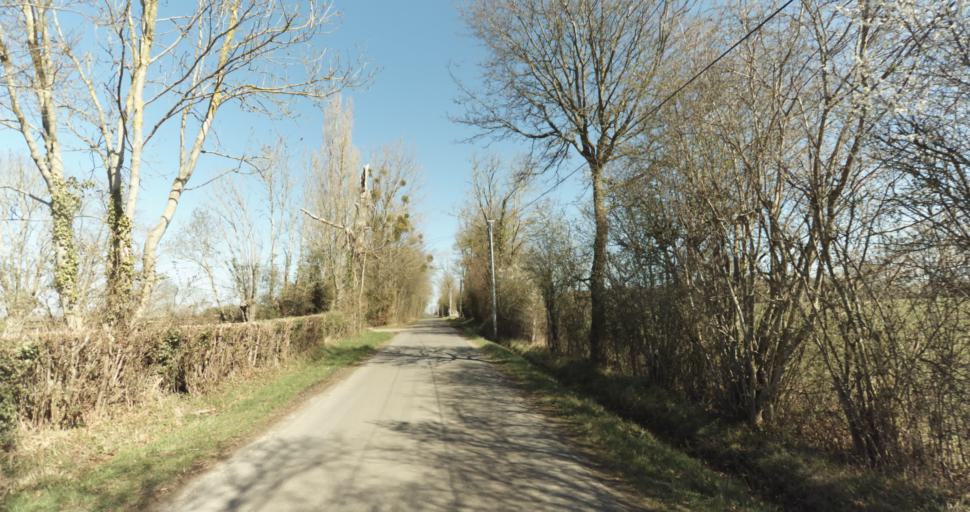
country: FR
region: Lower Normandy
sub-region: Departement du Calvados
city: Livarot
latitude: 49.0202
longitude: 0.0901
